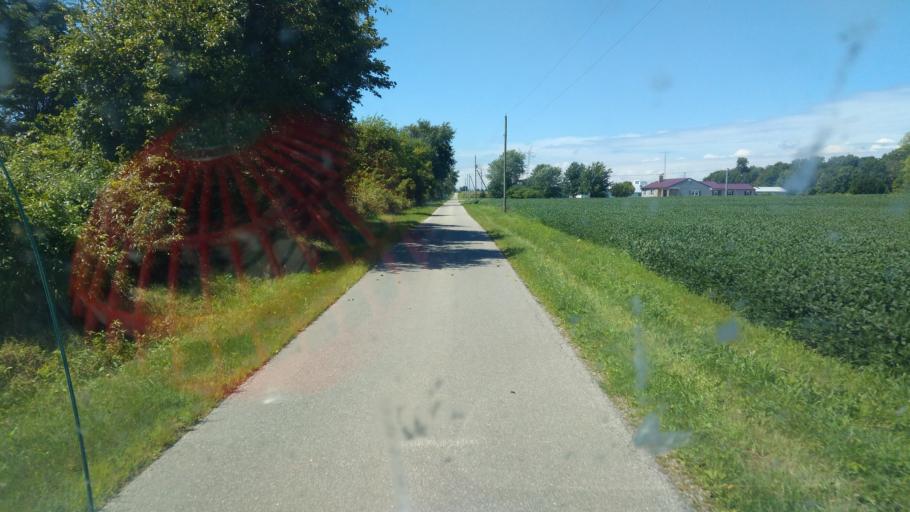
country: US
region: Ohio
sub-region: Crawford County
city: Bucyrus
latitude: 40.8125
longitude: -83.0298
